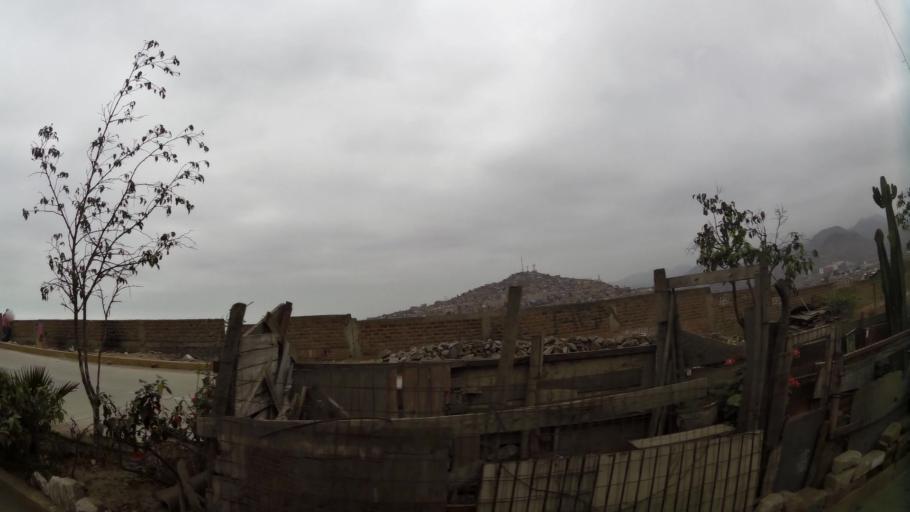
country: PE
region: Lima
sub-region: Lima
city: Surco
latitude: -12.1963
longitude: -76.9485
